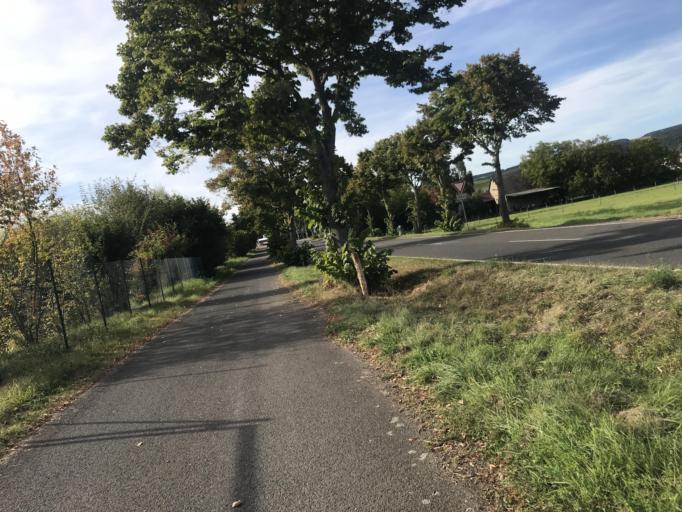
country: DE
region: Rheinland-Pfalz
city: Merxheim
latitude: 49.7928
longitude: 7.5691
